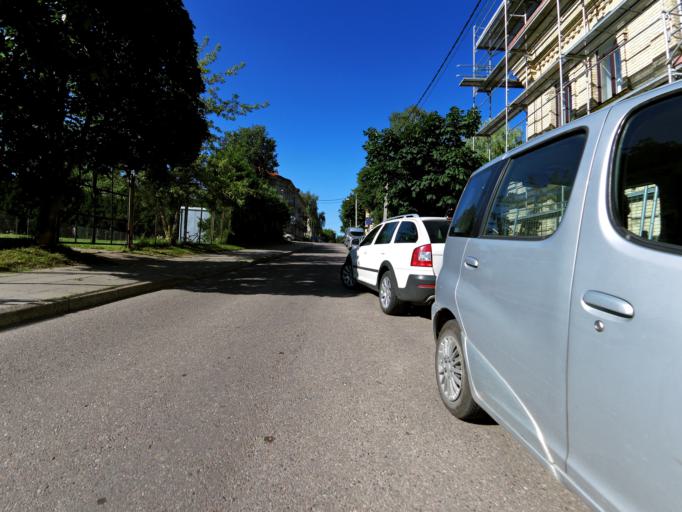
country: LT
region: Vilnius County
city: Naujamiestis
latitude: 54.6871
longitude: 25.2561
